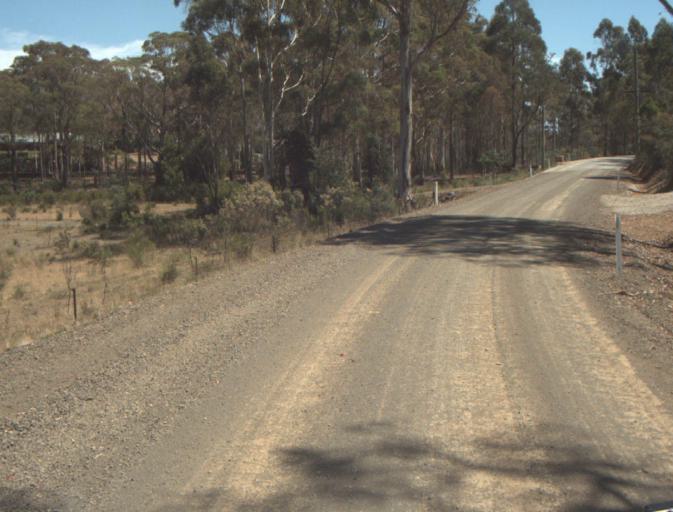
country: AU
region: Tasmania
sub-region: Launceston
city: Mayfield
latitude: -41.2773
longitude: 147.1105
